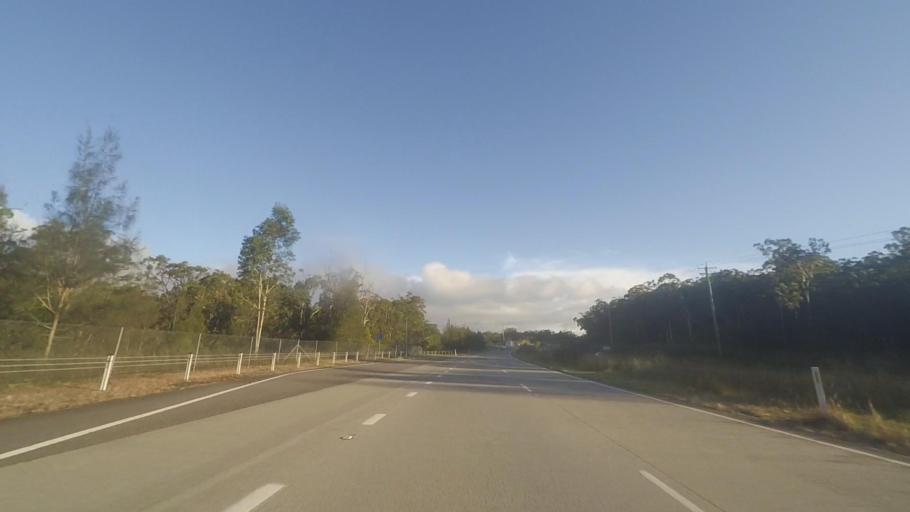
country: AU
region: New South Wales
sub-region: Great Lakes
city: Bulahdelah
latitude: -32.5006
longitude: 152.2097
